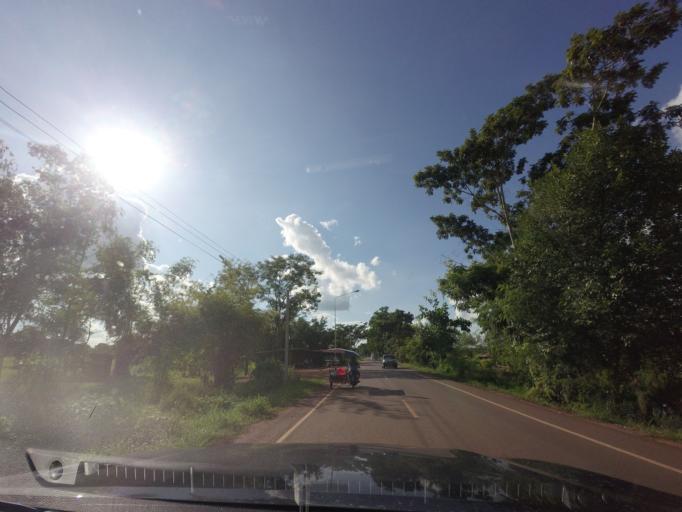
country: TH
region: Changwat Udon Thani
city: Ban Dung
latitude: 17.7392
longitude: 103.3460
